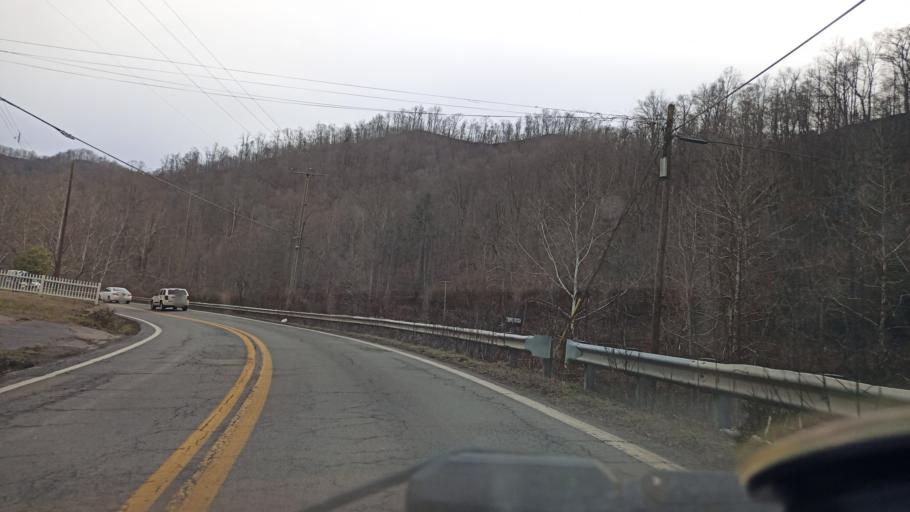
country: US
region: West Virginia
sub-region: Mingo County
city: Gilbert Creek
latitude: 37.6365
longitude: -81.8771
